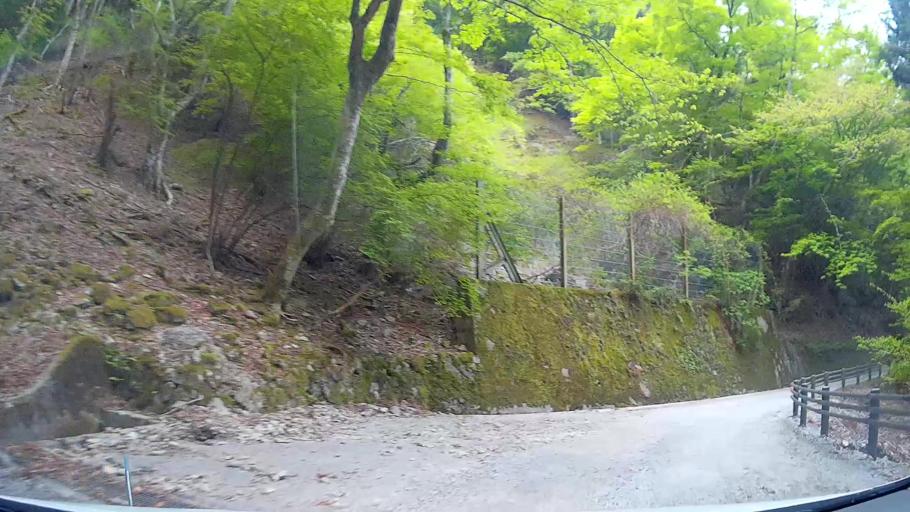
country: JP
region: Shizuoka
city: Shimoda
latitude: 34.8288
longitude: 138.9381
